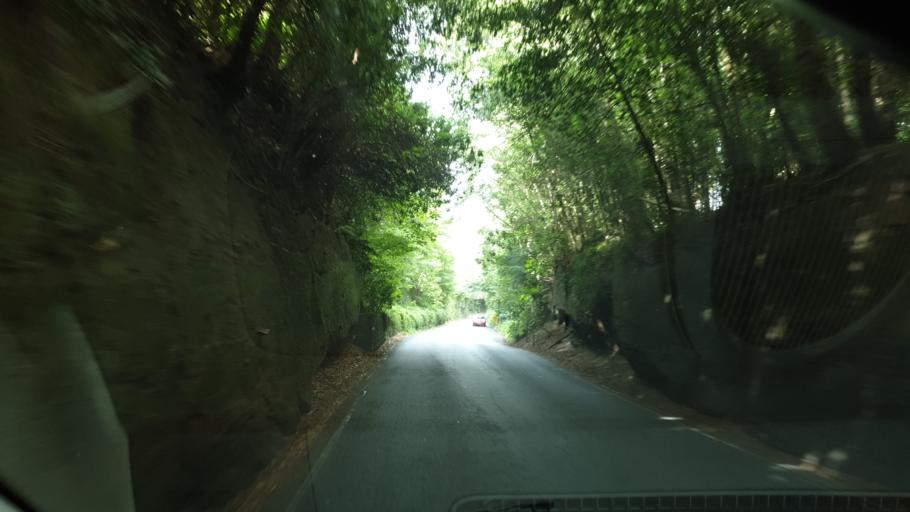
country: GB
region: England
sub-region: West Sussex
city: East Grinstead
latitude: 51.1289
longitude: -0.0039
